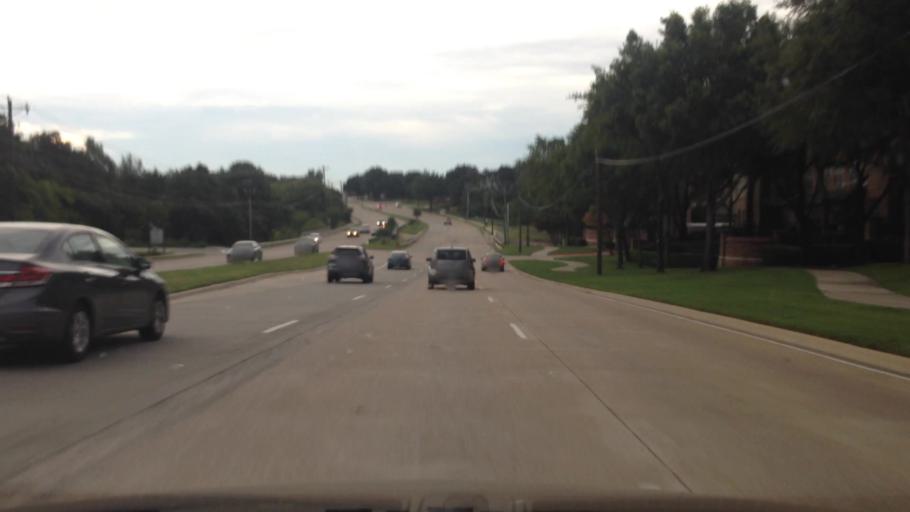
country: US
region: Texas
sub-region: Denton County
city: Flower Mound
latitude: 33.0081
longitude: -97.0452
